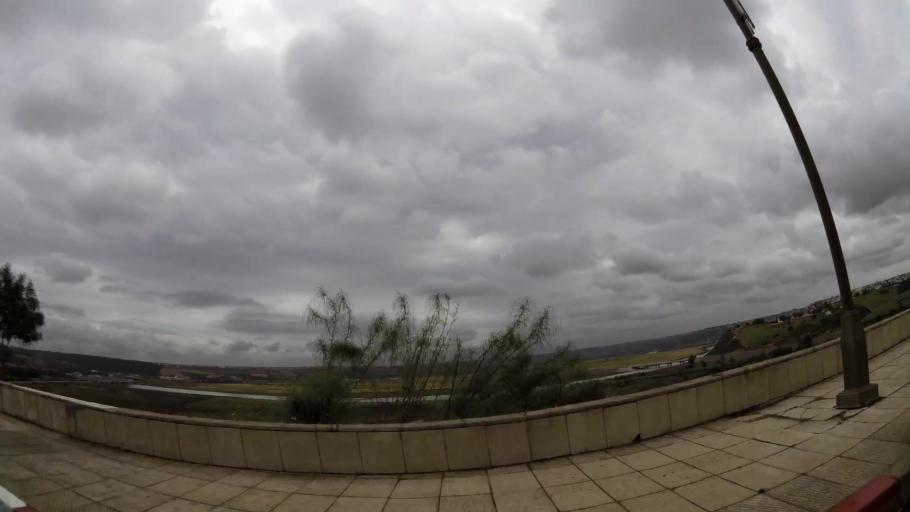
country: MA
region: Rabat-Sale-Zemmour-Zaer
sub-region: Rabat
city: Rabat
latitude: 34.0127
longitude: -6.8201
